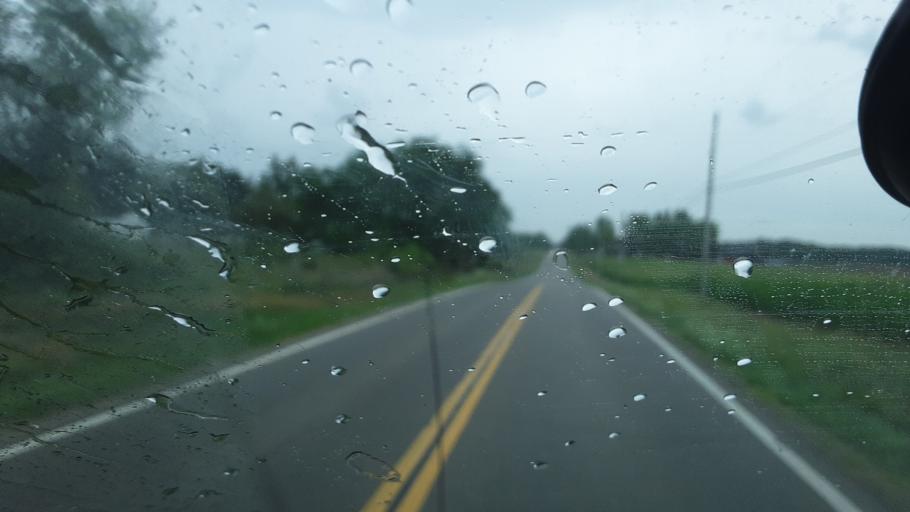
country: US
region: Ohio
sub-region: Williams County
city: Bryan
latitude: 41.4966
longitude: -84.6131
